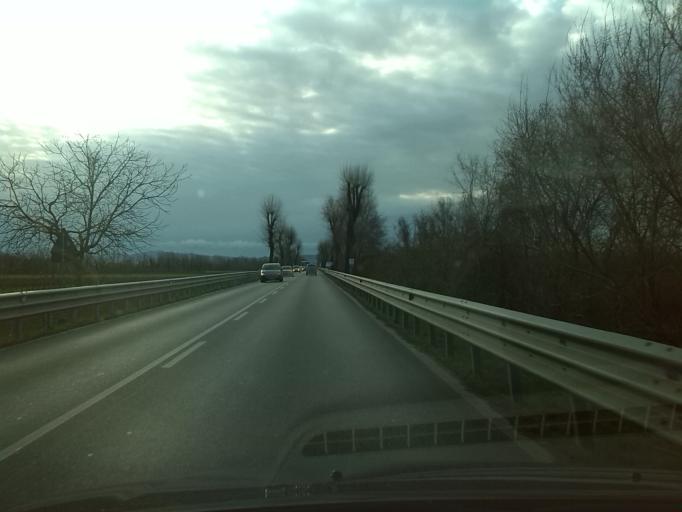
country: IT
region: Friuli Venezia Giulia
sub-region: Provincia di Udine
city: San Giovanni al Natisone
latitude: 45.9578
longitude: 13.4244
